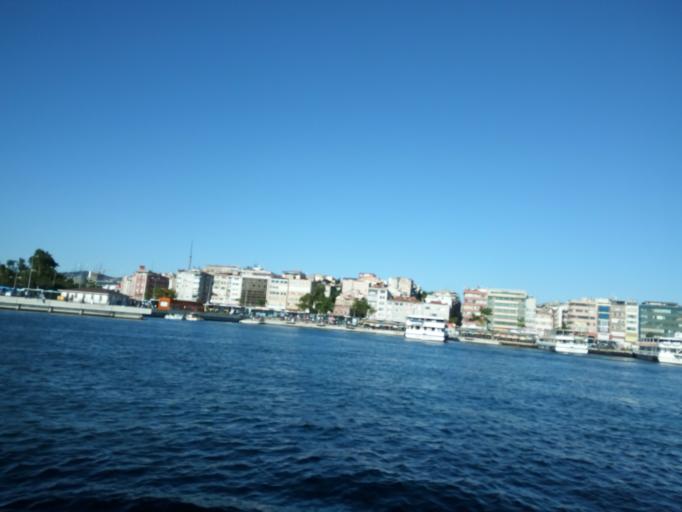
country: TR
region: Istanbul
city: UEskuedar
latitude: 40.9944
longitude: 29.0217
